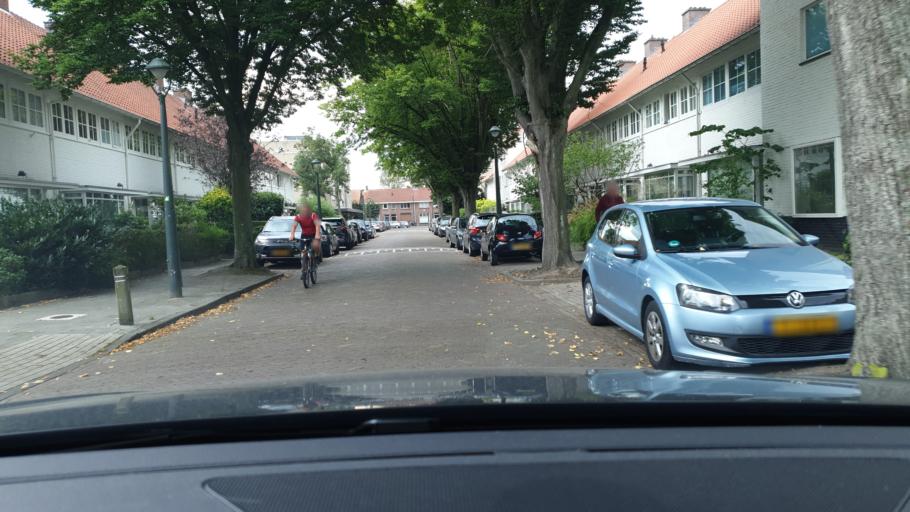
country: NL
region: North Brabant
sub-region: Gemeente Eindhoven
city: Lakerlopen
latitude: 51.4285
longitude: 5.4930
